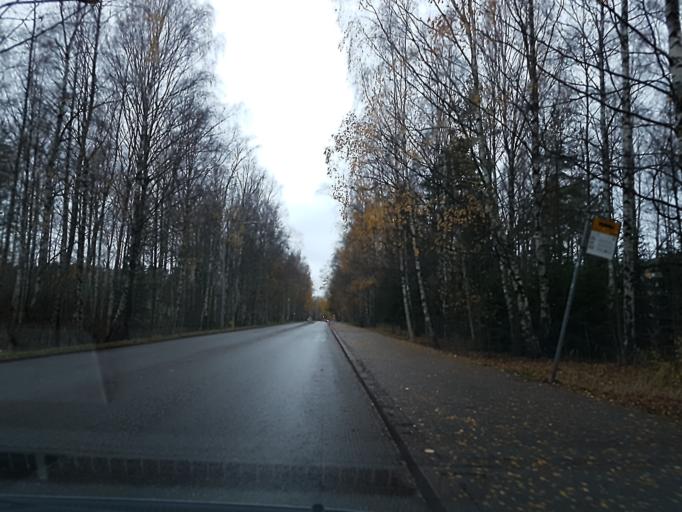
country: FI
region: Uusimaa
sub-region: Helsinki
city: Vantaa
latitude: 60.2307
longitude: 25.0856
